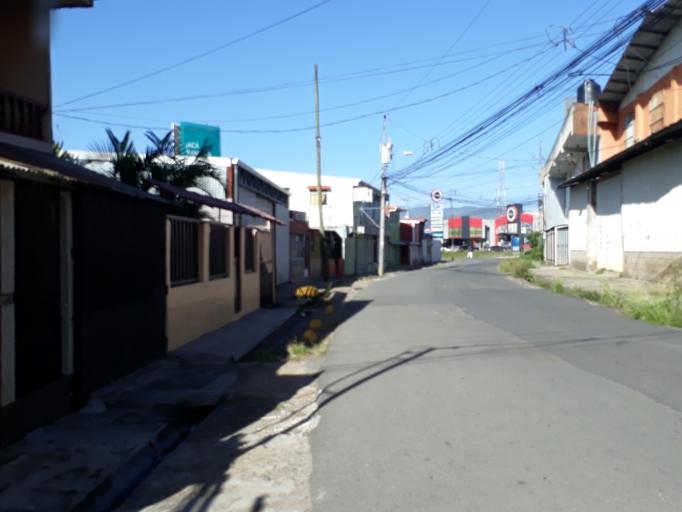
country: CR
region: Cartago
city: Cartago
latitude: 9.8730
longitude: -83.9433
